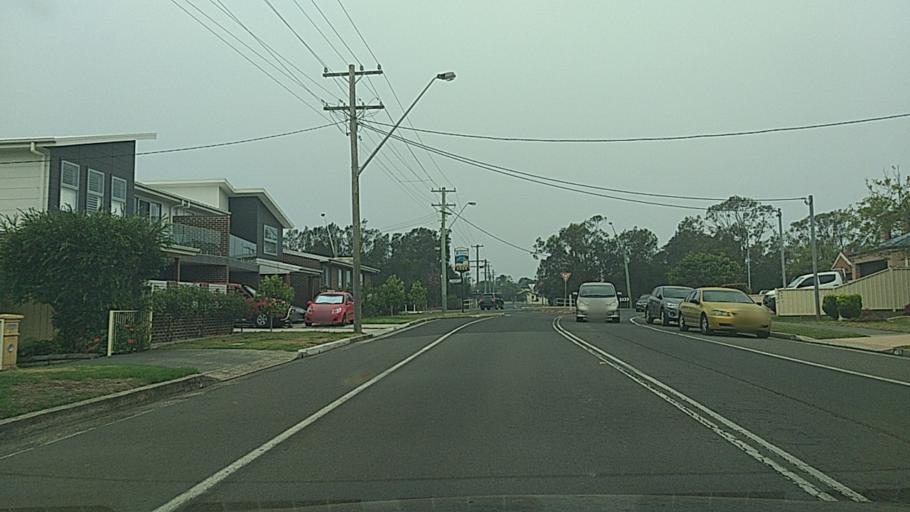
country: AU
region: New South Wales
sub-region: Shellharbour
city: Barrack Heights
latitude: -34.5643
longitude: 150.8641
